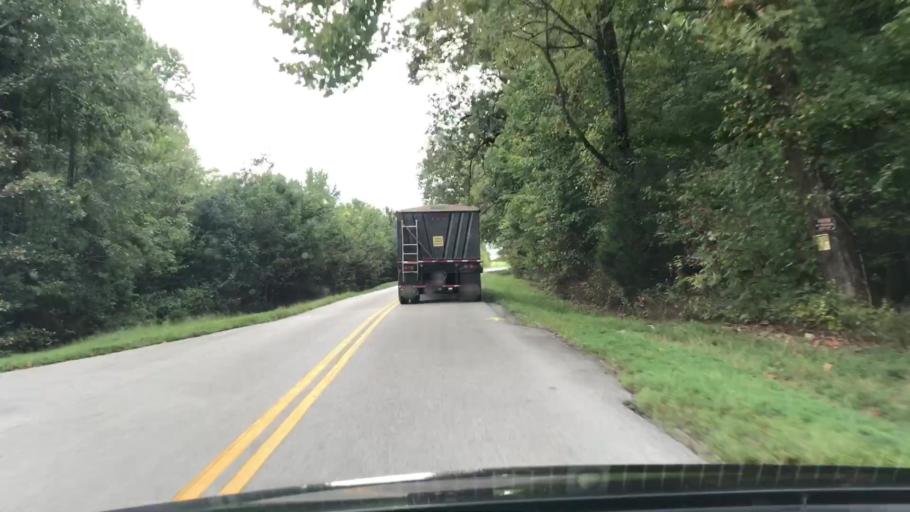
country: US
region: Kentucky
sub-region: Todd County
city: Guthrie
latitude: 36.6811
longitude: -87.0230
